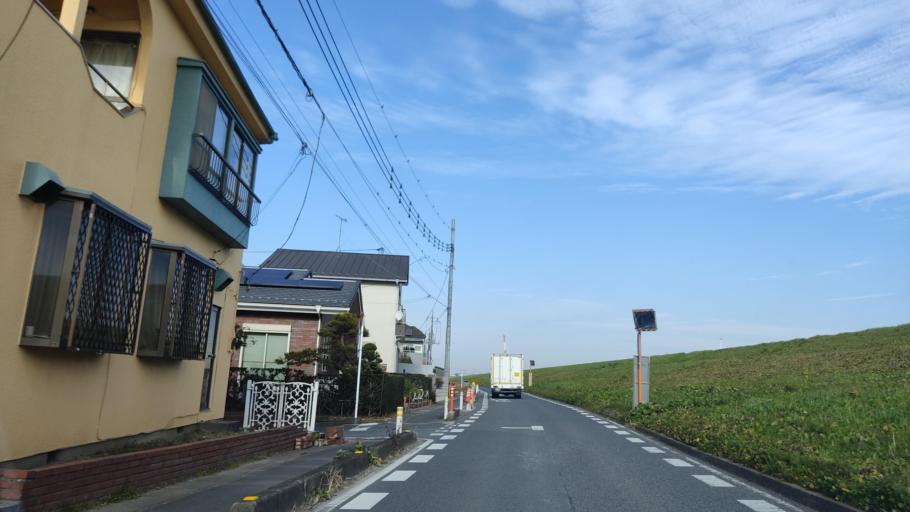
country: JP
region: Chiba
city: Nagareyama
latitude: 35.8536
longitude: 139.8912
